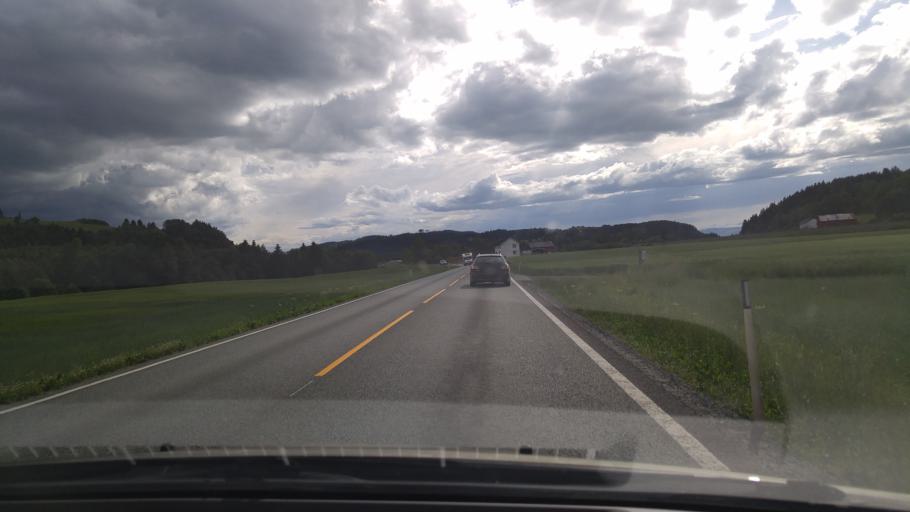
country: NO
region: Nord-Trondelag
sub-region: Verdal
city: Verdal
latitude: 63.8777
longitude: 11.4126
